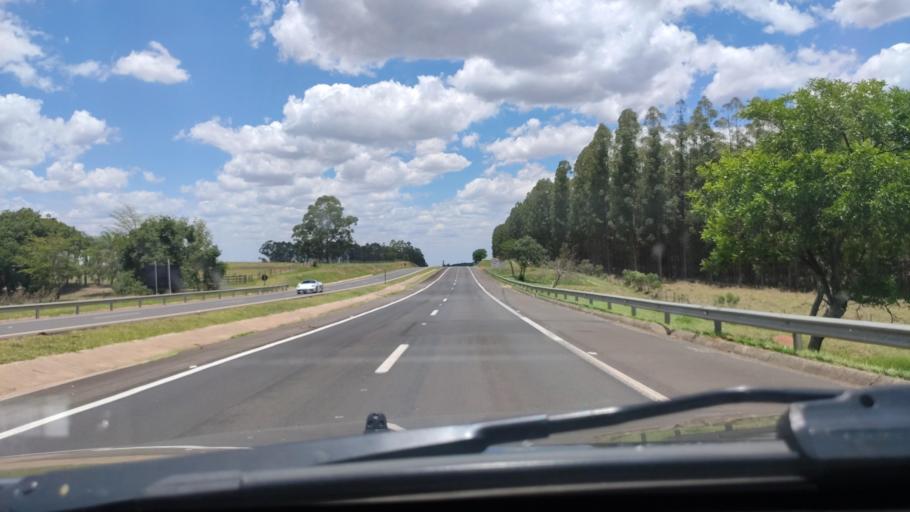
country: BR
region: Sao Paulo
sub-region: Duartina
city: Duartina
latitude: -22.5817
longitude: -49.3766
